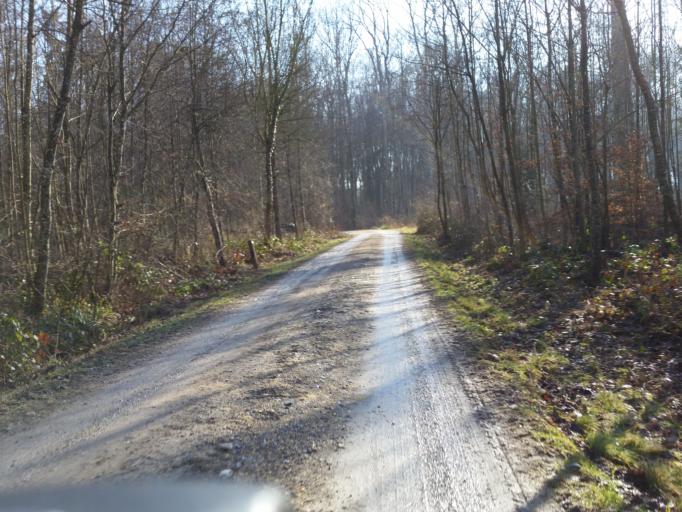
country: CH
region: Thurgau
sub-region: Arbon District
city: Uttwil
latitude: 47.5627
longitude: 9.3386
